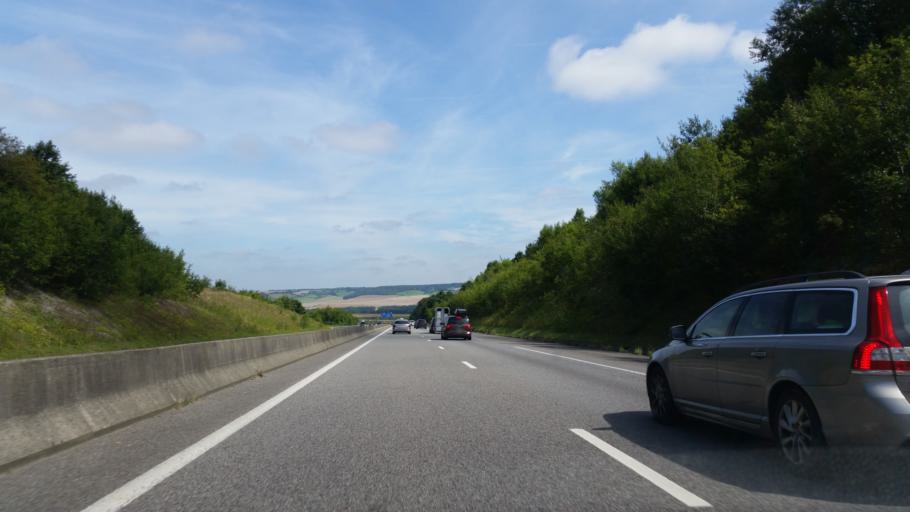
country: FR
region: Haute-Normandie
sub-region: Departement de la Seine-Maritime
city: Neufchatel-en-Bray
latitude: 49.7493
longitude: 1.4793
